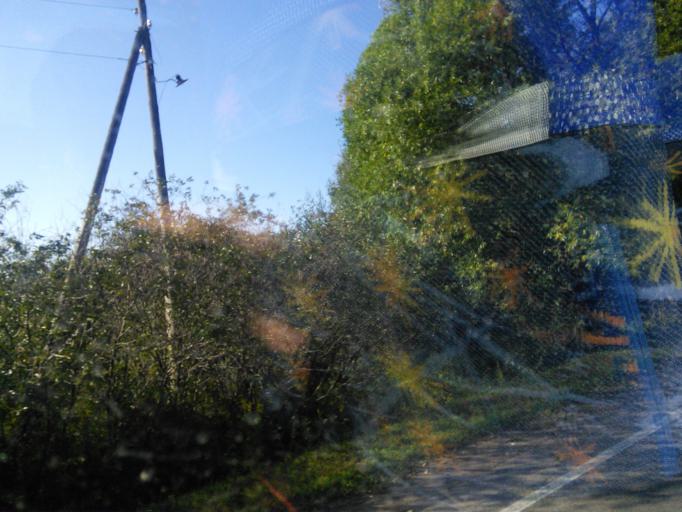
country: RU
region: Jaroslavl
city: Rybinsk
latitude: 58.2651
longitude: 38.8521
